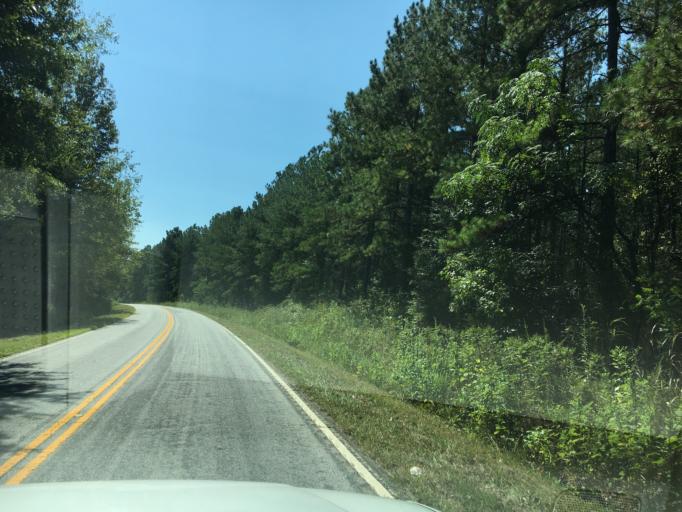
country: US
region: South Carolina
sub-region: Laurens County
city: Clinton
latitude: 34.4182
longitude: -81.8686
